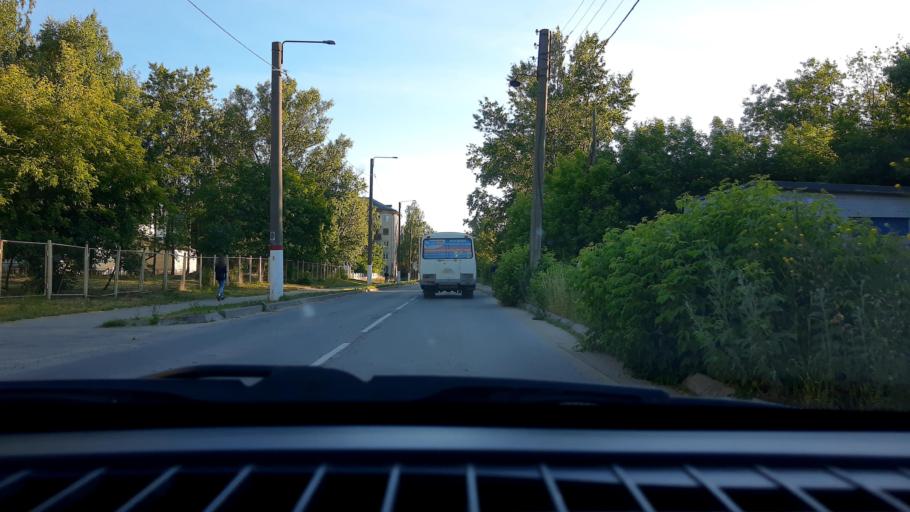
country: RU
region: Nizjnij Novgorod
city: Dzerzhinsk
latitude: 56.2434
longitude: 43.4881
